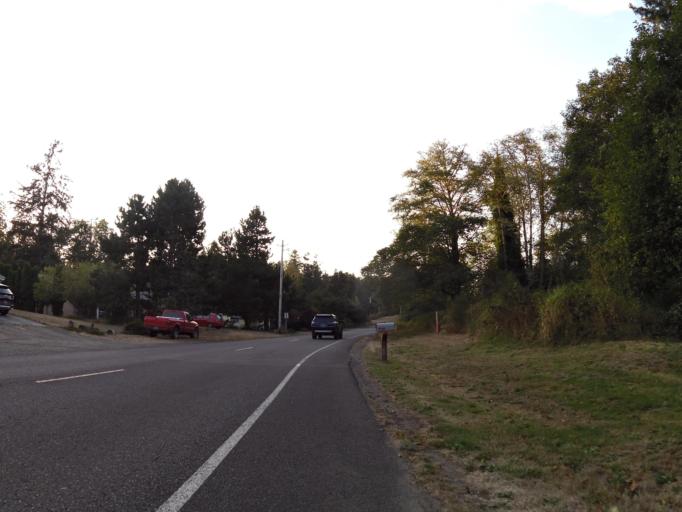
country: US
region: Oregon
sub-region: Clatsop County
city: Warrenton
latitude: 46.1585
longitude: -123.9443
